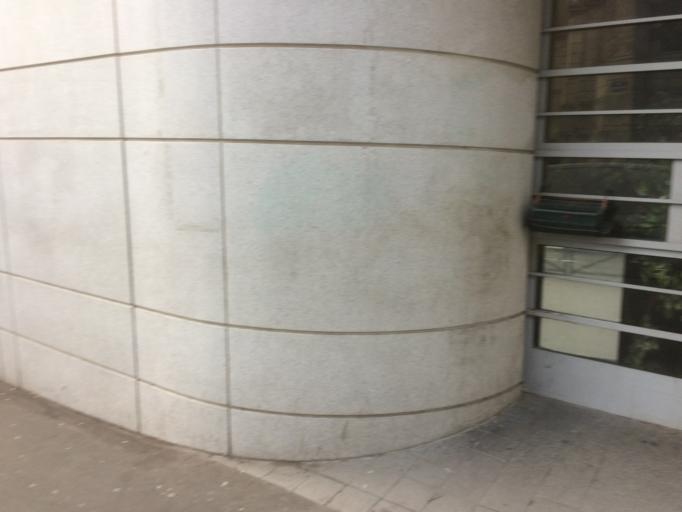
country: FR
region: Ile-de-France
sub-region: Departement de Seine-Saint-Denis
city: Le Pre-Saint-Gervais
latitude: 48.8688
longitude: 2.3869
